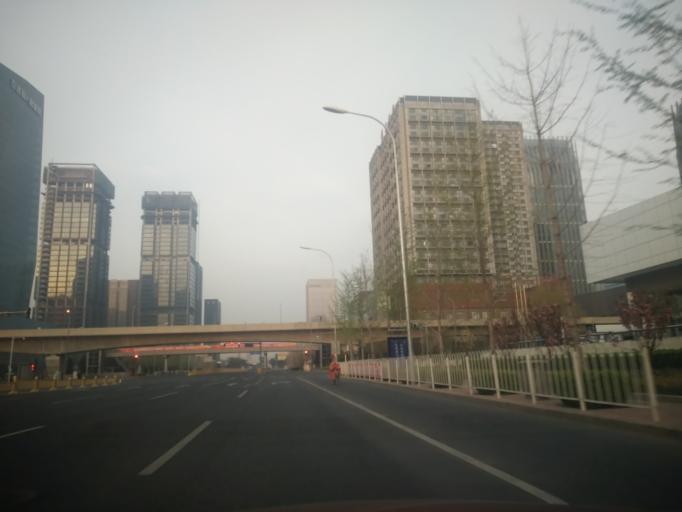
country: CN
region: Beijing
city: Jiugong
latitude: 39.7936
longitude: 116.5077
